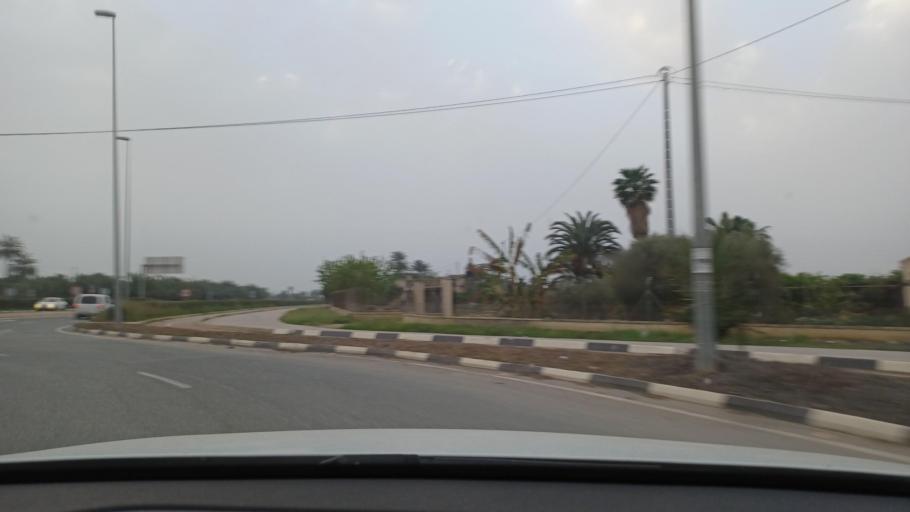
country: ES
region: Valencia
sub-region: Provincia de Alicante
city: Elche
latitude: 38.1874
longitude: -0.7016
